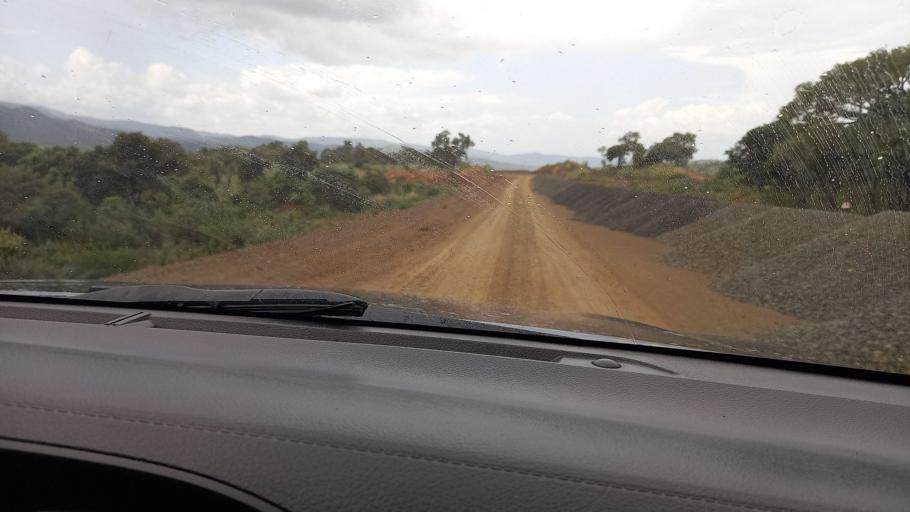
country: ET
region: Southern Nations, Nationalities, and People's Region
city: Mizan Teferi
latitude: 6.1834
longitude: 35.6913
